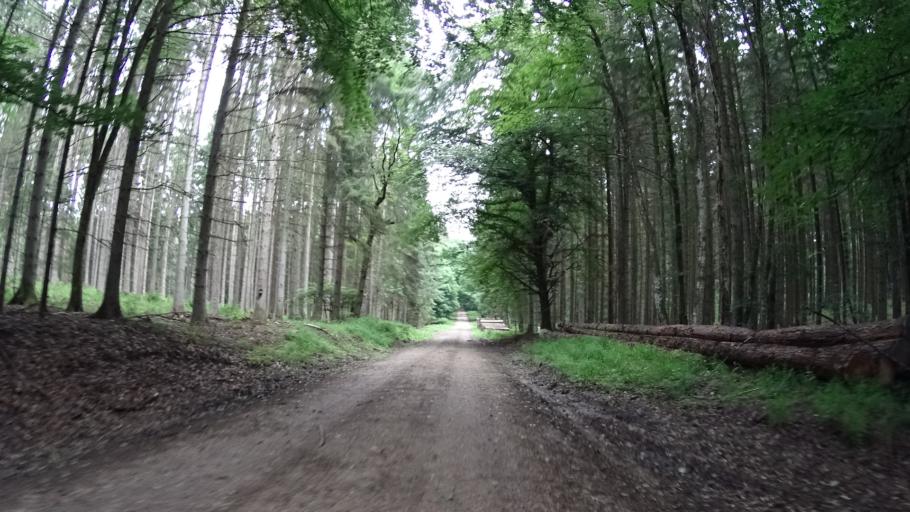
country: DE
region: Bavaria
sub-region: Upper Bavaria
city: Stammham
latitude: 48.8784
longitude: 11.5229
